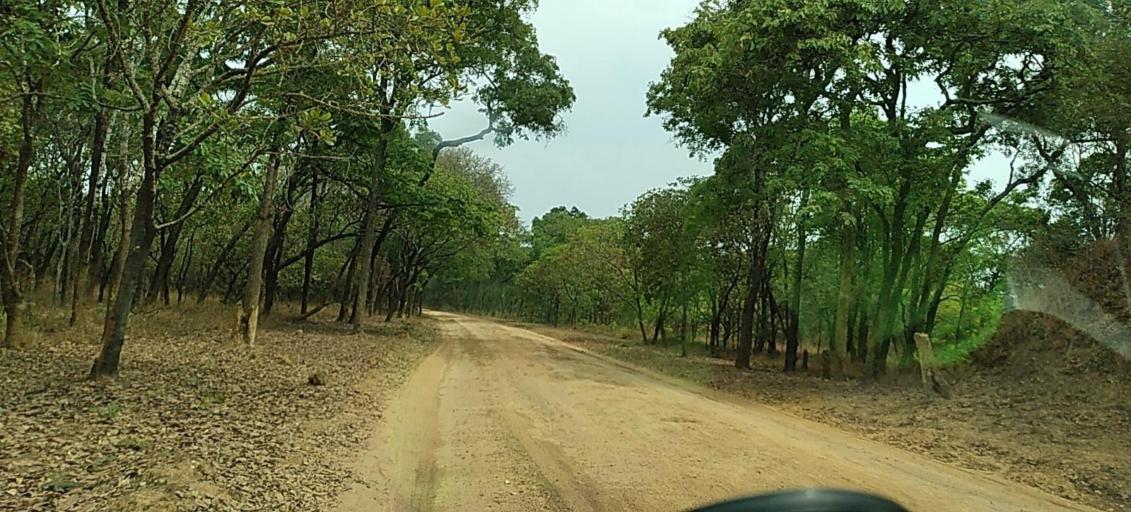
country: ZM
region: North-Western
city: Solwezi
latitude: -12.9450
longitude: 26.5588
